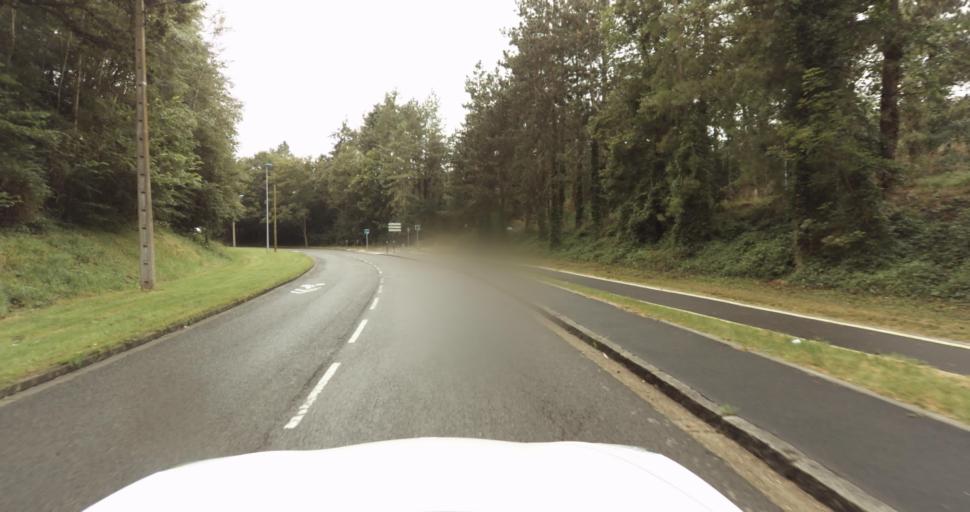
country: FR
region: Haute-Normandie
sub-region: Departement de l'Eure
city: Evreux
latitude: 49.0345
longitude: 1.1487
